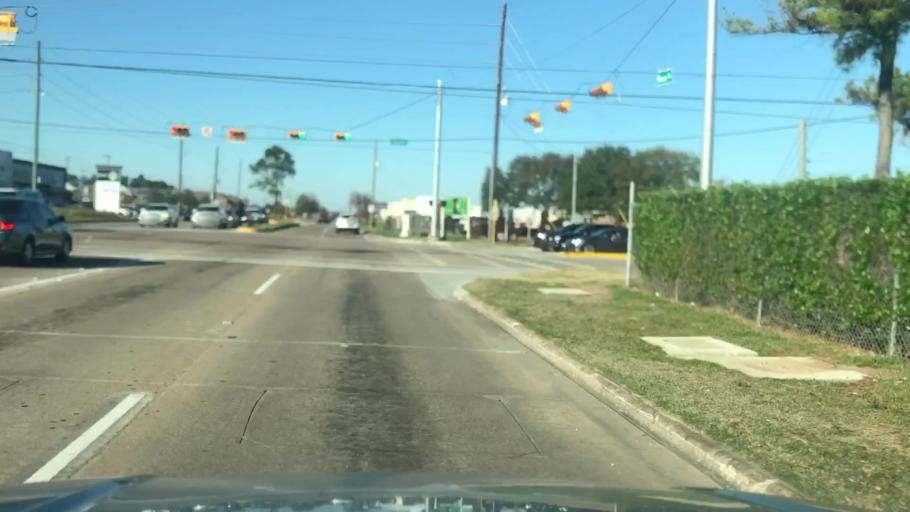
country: US
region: Texas
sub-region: Fort Bend County
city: Cinco Ranch
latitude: 29.8017
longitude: -95.7519
